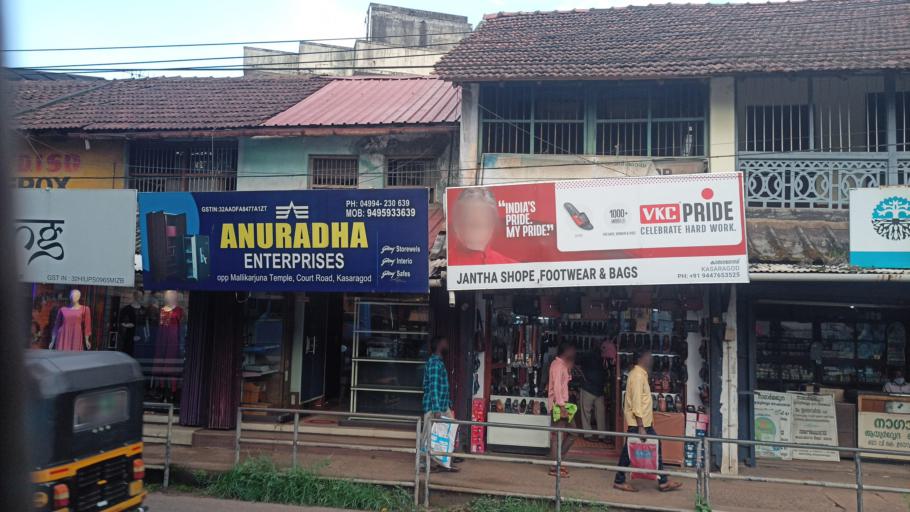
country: IN
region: Kerala
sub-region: Kasaragod District
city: Kasaragod
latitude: 12.5008
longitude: 74.9869
